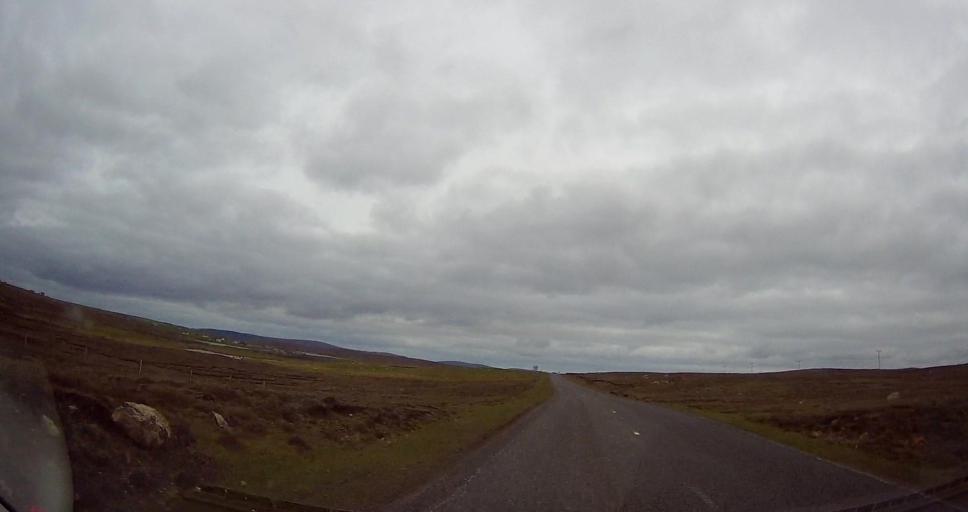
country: GB
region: Scotland
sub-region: Shetland Islands
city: Shetland
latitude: 60.7050
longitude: -0.9199
